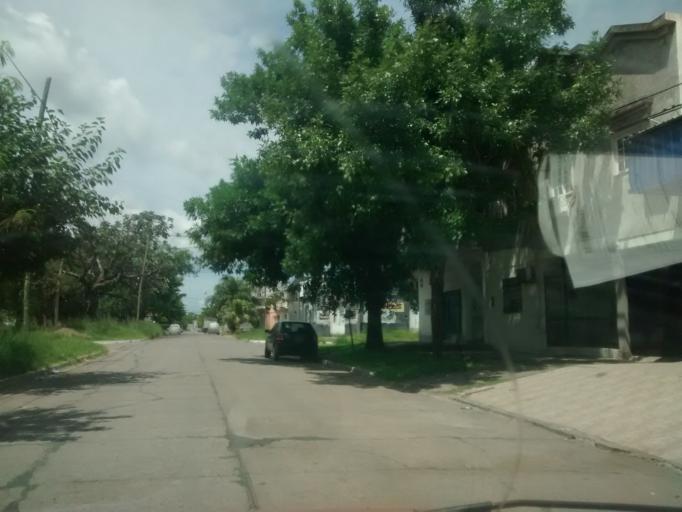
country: AR
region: Chaco
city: Resistencia
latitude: -27.4453
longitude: -58.9960
